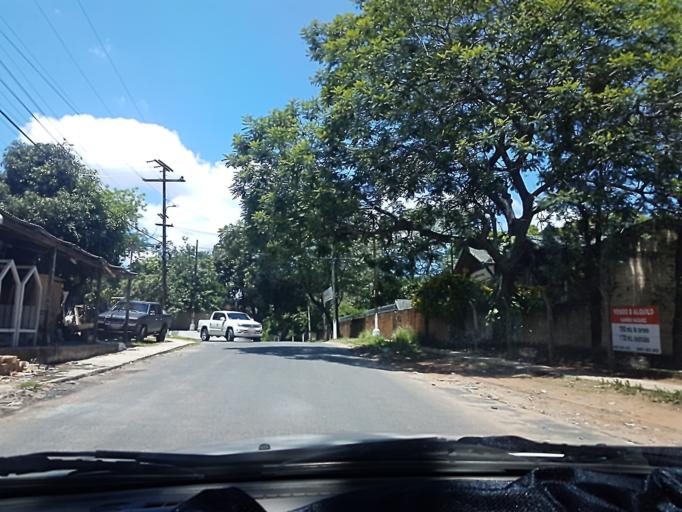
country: PY
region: Central
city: Lambare
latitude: -25.3544
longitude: -57.6292
